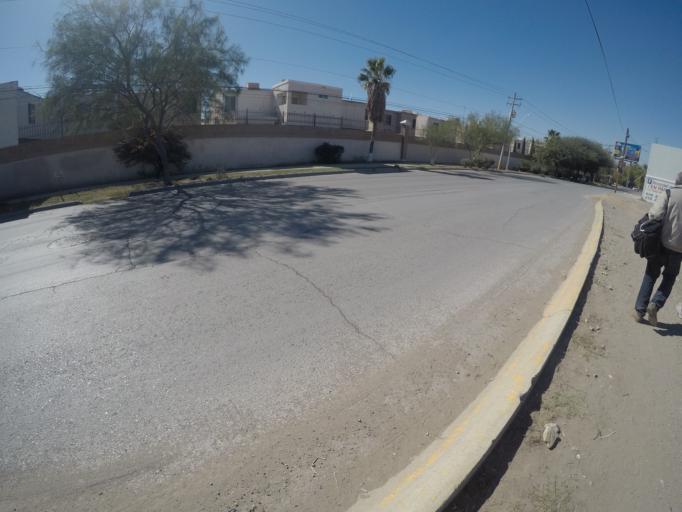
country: US
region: Texas
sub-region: El Paso County
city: Socorro
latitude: 31.6944
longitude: -106.3758
